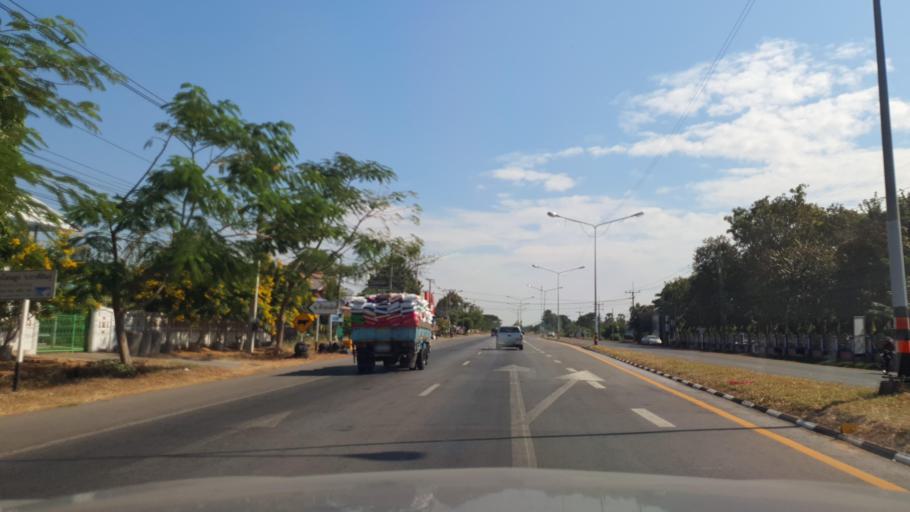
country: TH
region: Maha Sarakham
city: Chiang Yuen
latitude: 16.3789
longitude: 103.1892
